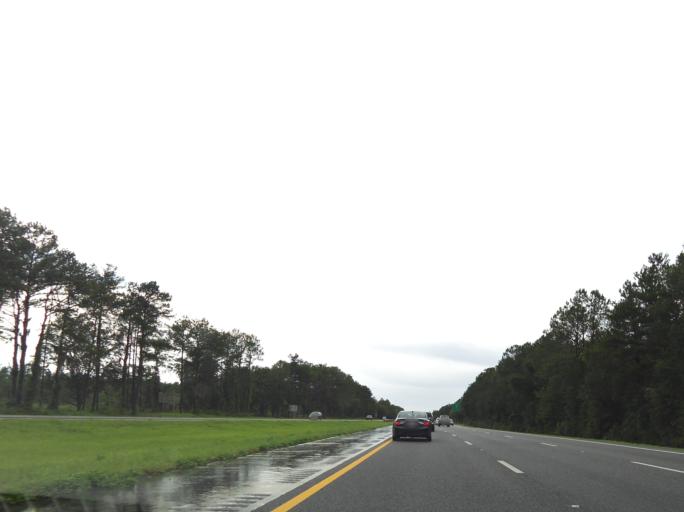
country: US
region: Florida
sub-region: Hamilton County
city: Jasper
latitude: 30.4399
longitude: -82.9183
